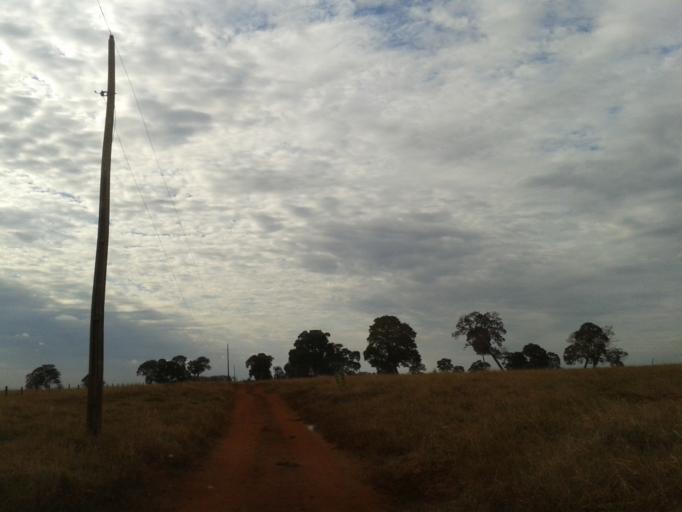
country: BR
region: Minas Gerais
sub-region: Santa Vitoria
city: Santa Vitoria
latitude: -18.7328
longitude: -50.2449
